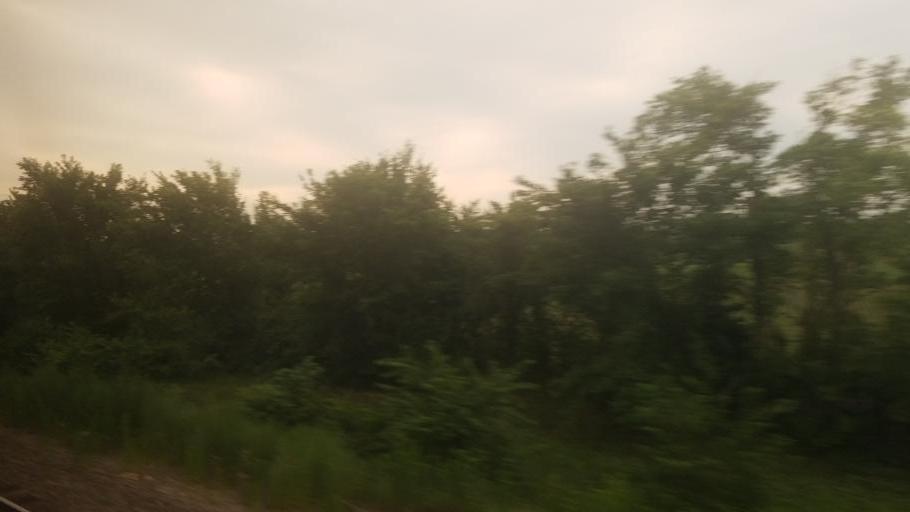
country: US
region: Kansas
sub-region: Chase County
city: Cottonwood Falls
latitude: 38.3842
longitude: -96.5078
